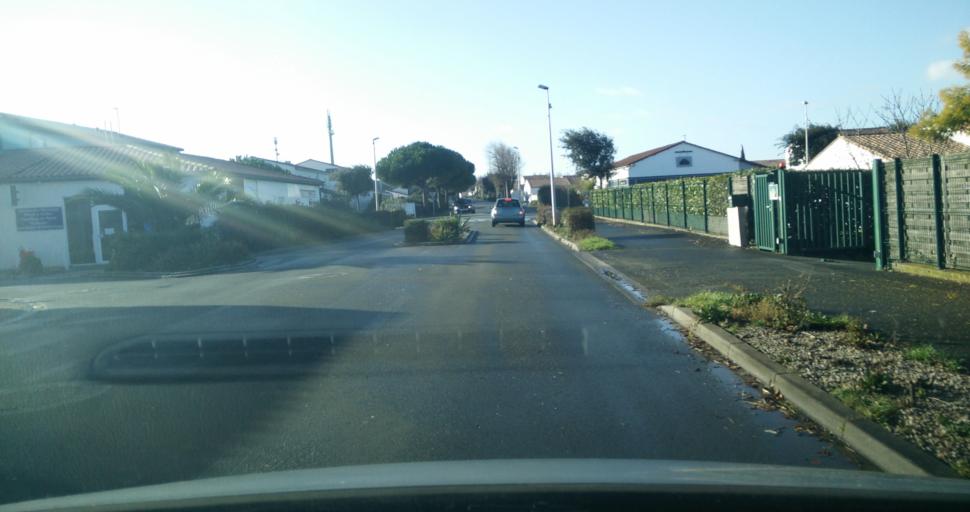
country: FR
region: Poitou-Charentes
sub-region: Departement de la Charente-Maritime
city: Saint-Martin-de-Re
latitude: 46.1976
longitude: -1.3549
